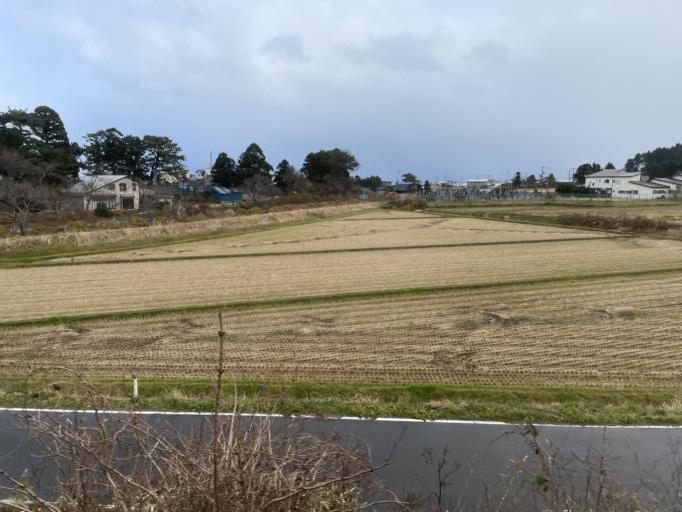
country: JP
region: Aomori
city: Aomori Shi
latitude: 41.0166
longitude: 140.6452
